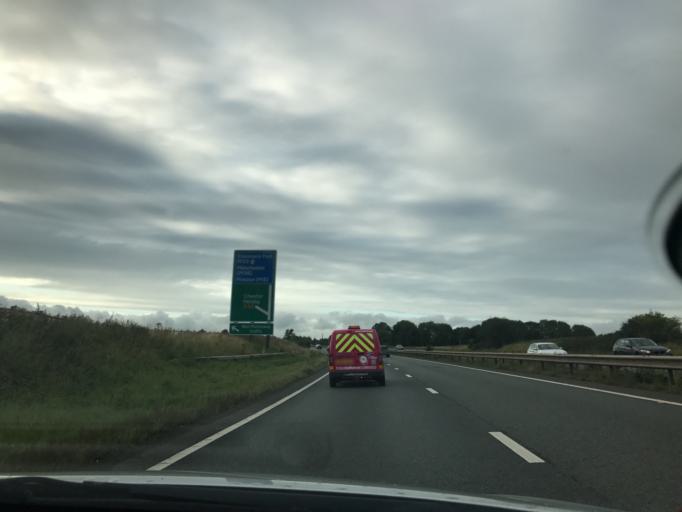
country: GB
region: England
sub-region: Cheshire West and Chester
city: Guilden Sutton
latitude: 53.2077
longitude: -2.8457
